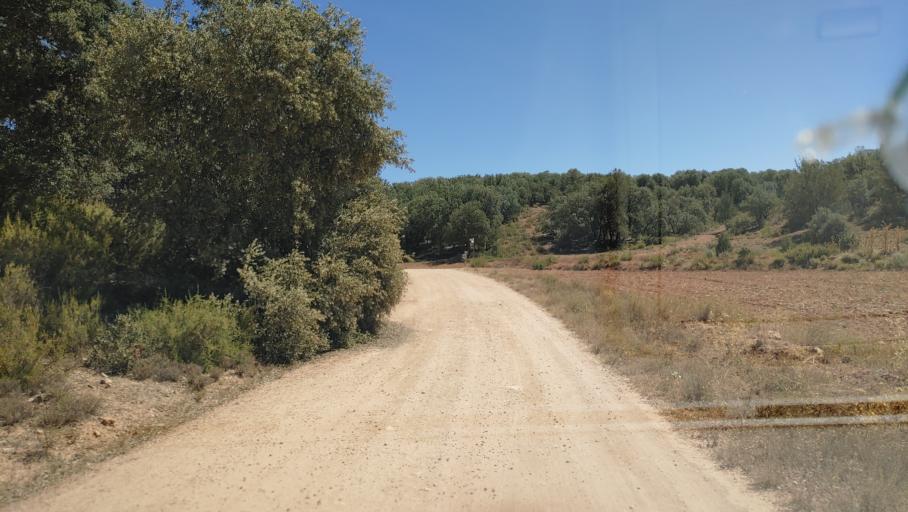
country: ES
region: Castille-La Mancha
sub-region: Provincia de Albacete
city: Ossa de Montiel
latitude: 38.9187
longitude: -2.8071
